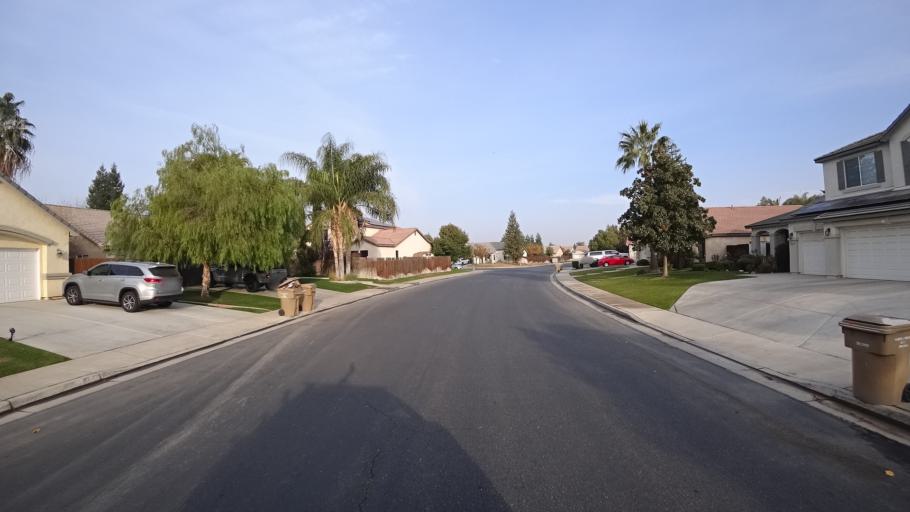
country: US
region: California
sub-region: Kern County
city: Greenacres
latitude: 35.4215
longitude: -119.1227
